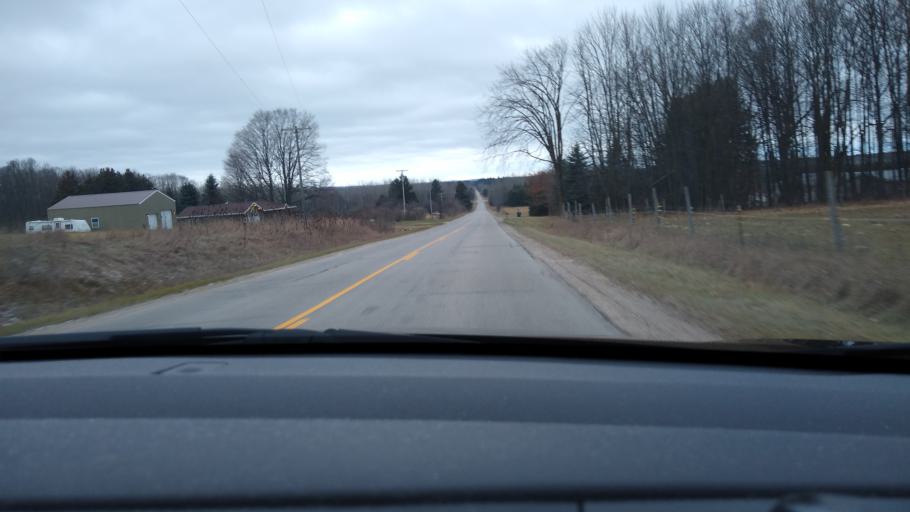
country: US
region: Michigan
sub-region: Missaukee County
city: Lake City
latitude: 44.3291
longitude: -85.0549
